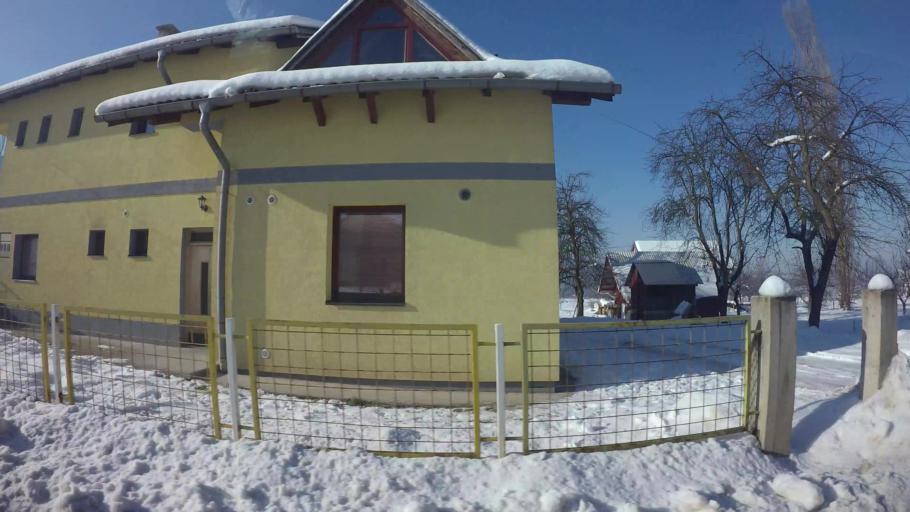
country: BA
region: Federation of Bosnia and Herzegovina
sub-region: Kanton Sarajevo
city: Sarajevo
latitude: 43.8179
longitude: 18.3826
